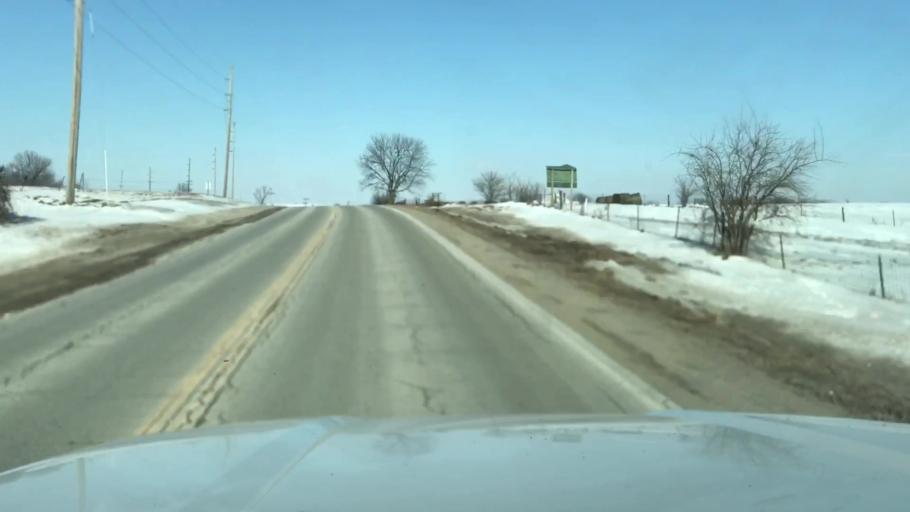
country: US
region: Missouri
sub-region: Andrew County
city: Savannah
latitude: 39.9562
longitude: -94.8495
